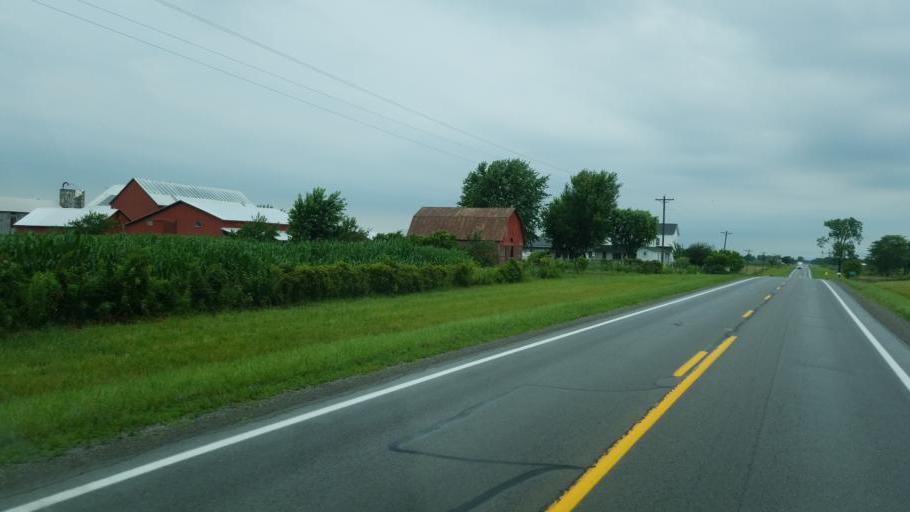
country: US
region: Ohio
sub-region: Hardin County
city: Kenton
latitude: 40.5701
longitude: -83.5899
